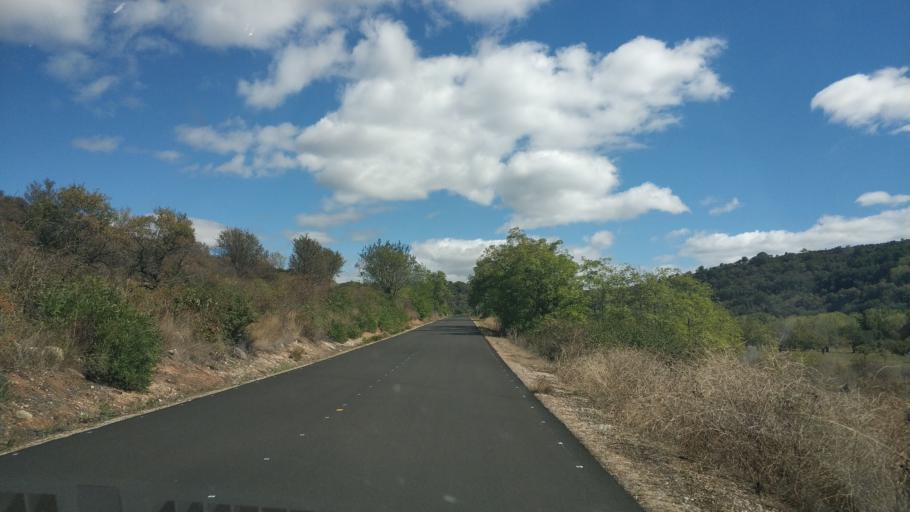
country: ES
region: Castille and Leon
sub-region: Provincia de Burgos
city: Covarrubias
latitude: 42.0481
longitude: -3.5342
